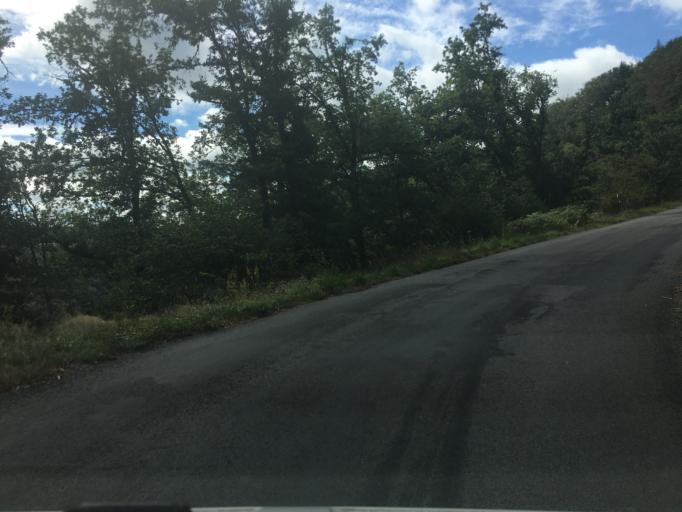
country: FR
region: Auvergne
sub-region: Departement du Cantal
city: Champagnac
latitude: 45.4326
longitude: 2.3973
